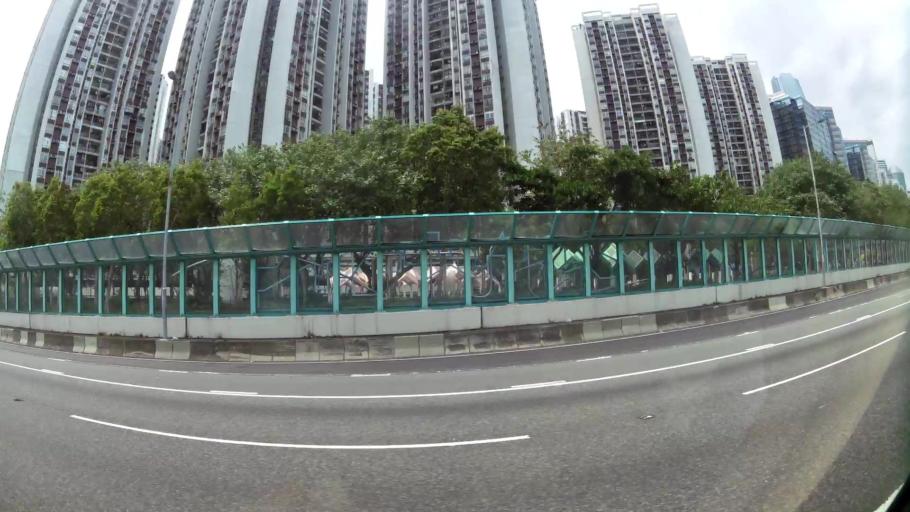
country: HK
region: Kowloon City
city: Kowloon
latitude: 22.2886
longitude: 114.2198
